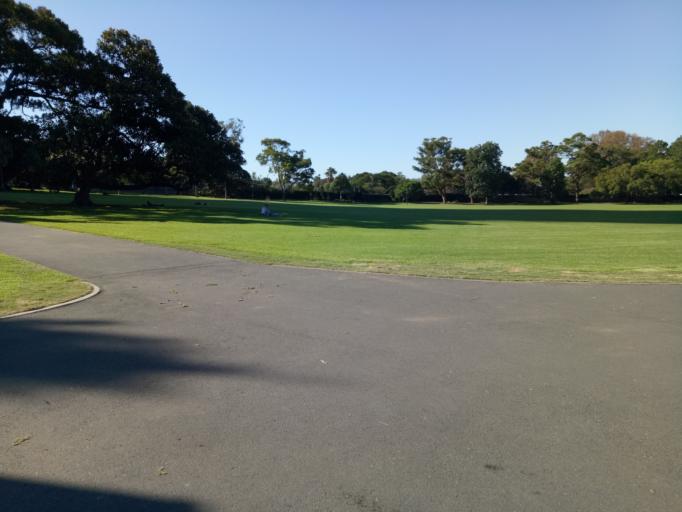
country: AU
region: New South Wales
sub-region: City of Sydney
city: Sydney
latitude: -33.8680
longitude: 151.2141
